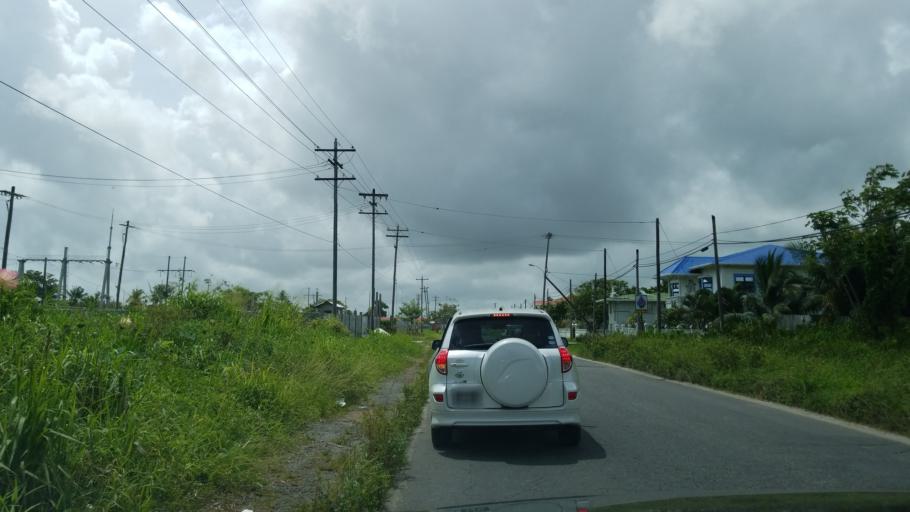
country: GY
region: Demerara-Mahaica
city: Georgetown
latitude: 6.7877
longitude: -58.1458
